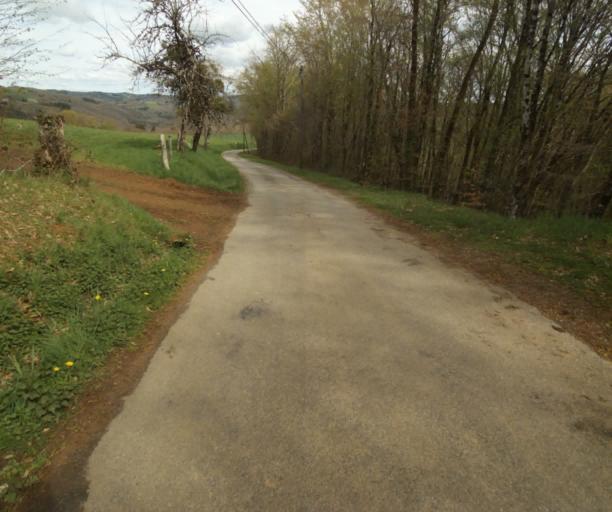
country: FR
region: Limousin
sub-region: Departement de la Correze
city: Laguenne
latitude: 45.2268
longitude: 1.8488
